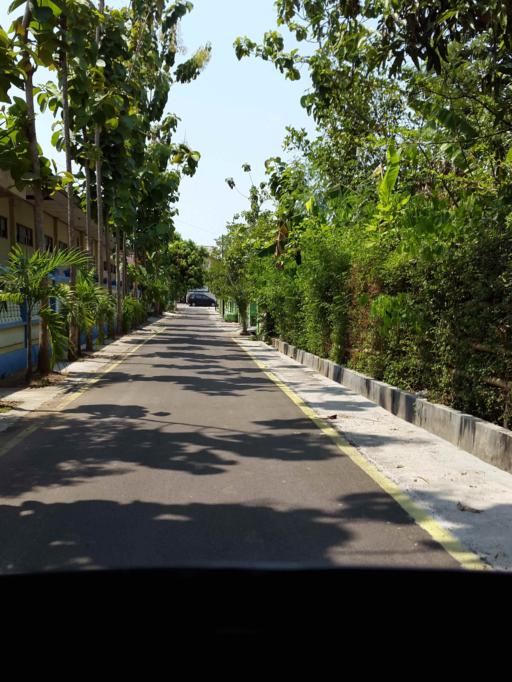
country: ID
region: Central Java
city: Jaten
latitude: -7.5957
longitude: 110.9560
